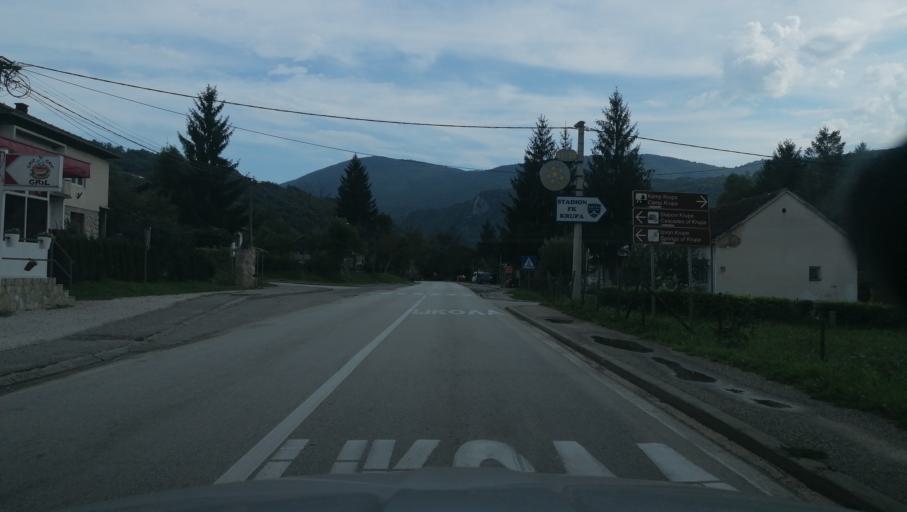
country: BA
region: Republika Srpska
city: Hiseti
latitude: 44.6172
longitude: 17.1444
